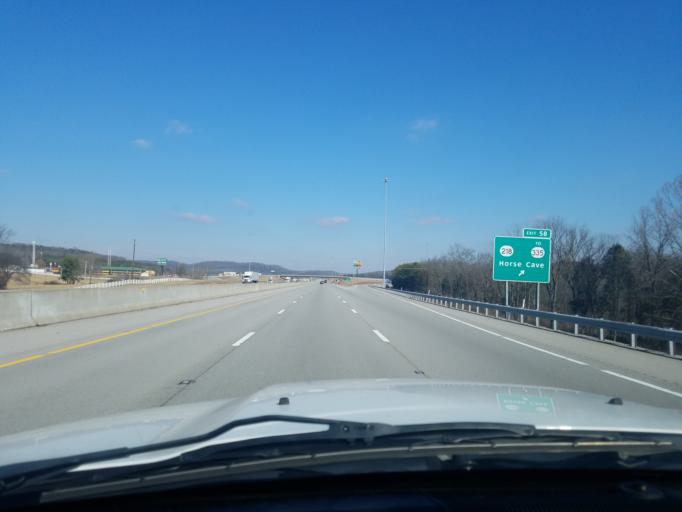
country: US
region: Kentucky
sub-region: Hart County
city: Horse Cave
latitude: 37.1962
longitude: -85.9381
